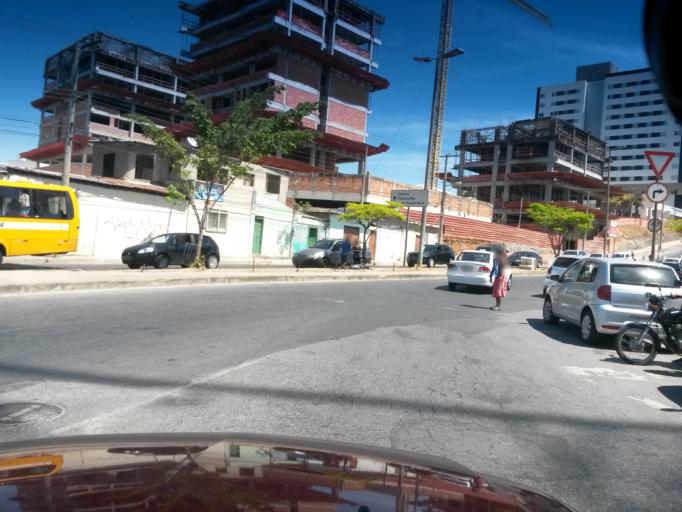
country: BR
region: Minas Gerais
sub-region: Belo Horizonte
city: Belo Horizonte
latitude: -19.8911
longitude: -43.9666
